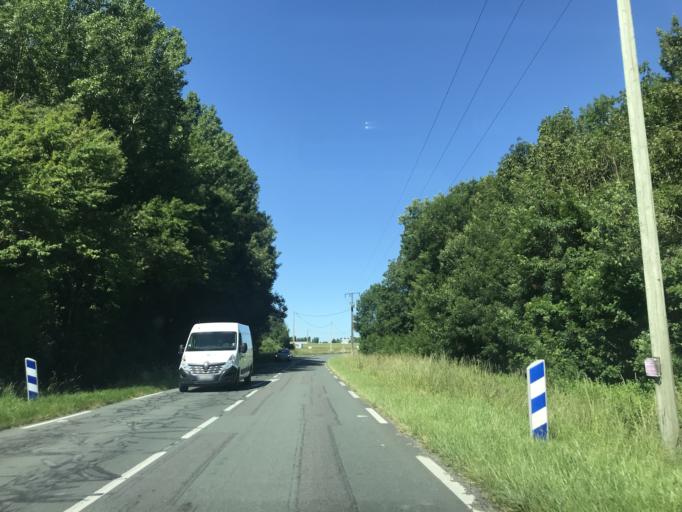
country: FR
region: Poitou-Charentes
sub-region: Departement de la Charente-Maritime
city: Perignac
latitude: 45.5757
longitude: -0.4808
